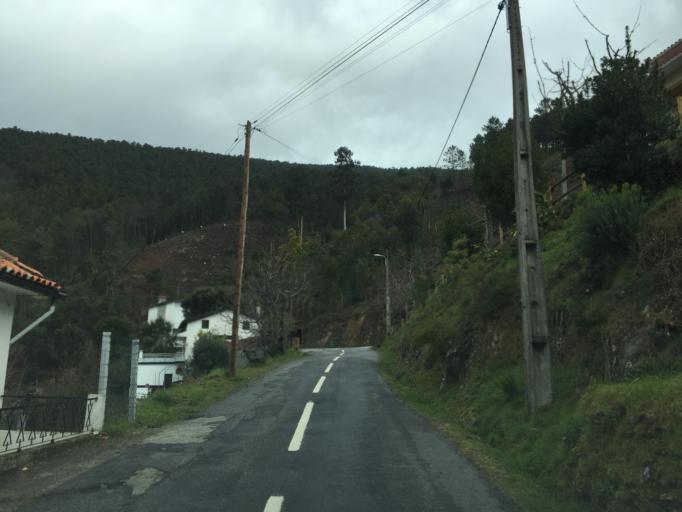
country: PT
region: Guarda
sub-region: Seia
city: Seia
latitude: 40.3204
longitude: -7.7310
